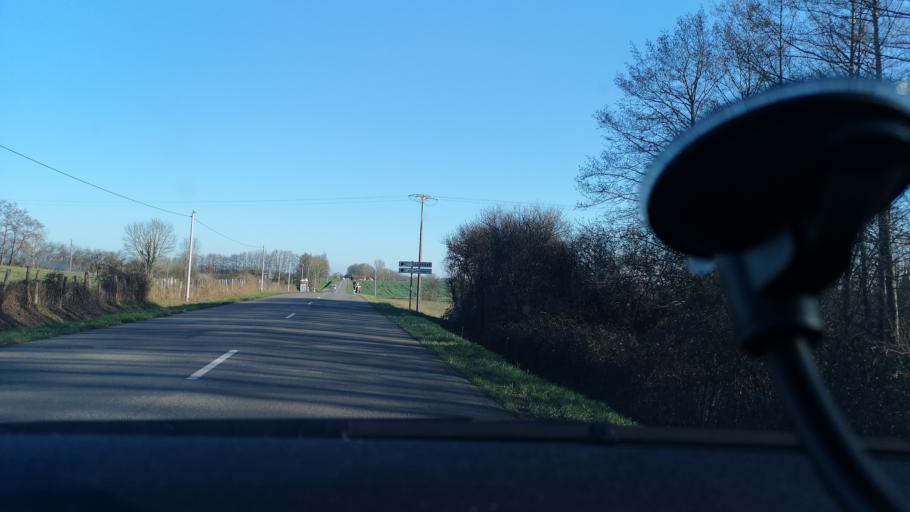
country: FR
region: Bourgogne
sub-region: Departement de Saone-et-Loire
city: Mervans
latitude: 46.7477
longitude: 5.1617
